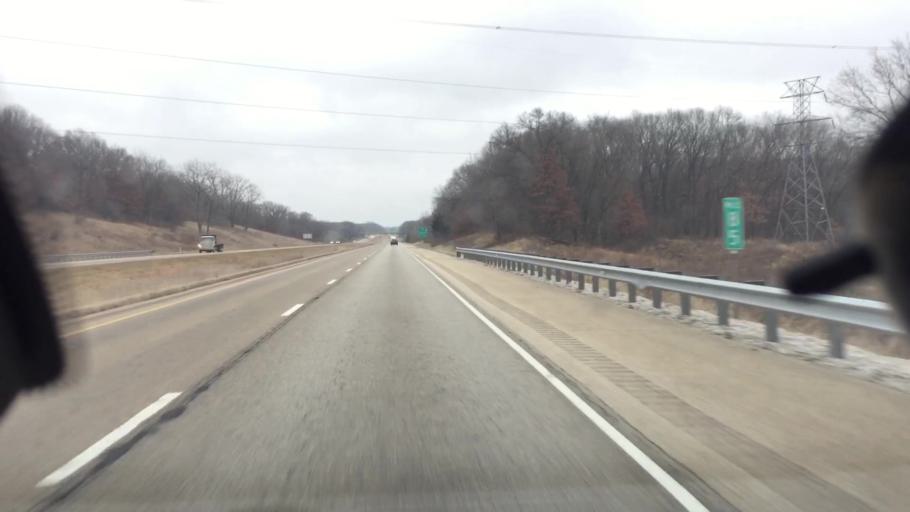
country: US
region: Illinois
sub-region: Peoria County
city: Bellevue
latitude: 40.7529
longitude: -89.6999
